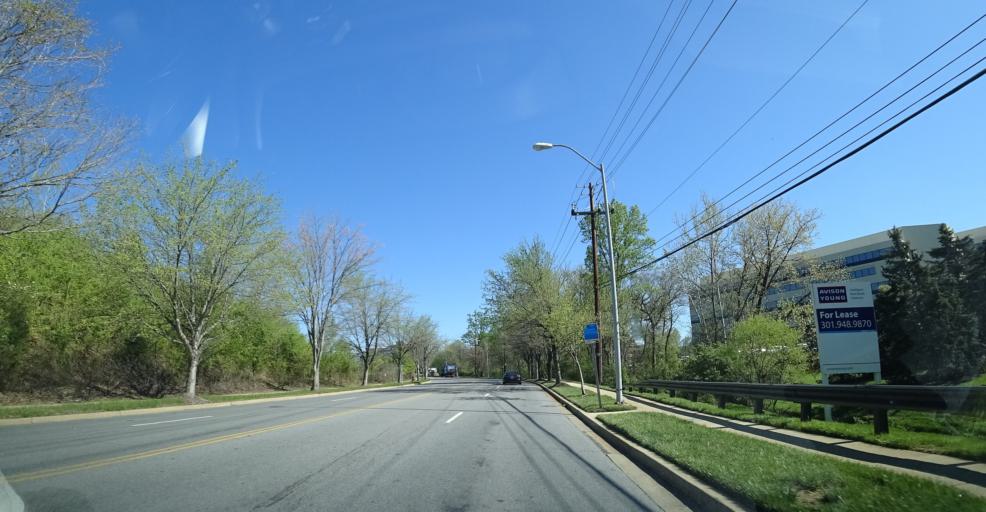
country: US
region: Maryland
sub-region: Montgomery County
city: Derwood
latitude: 39.0973
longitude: -77.1813
